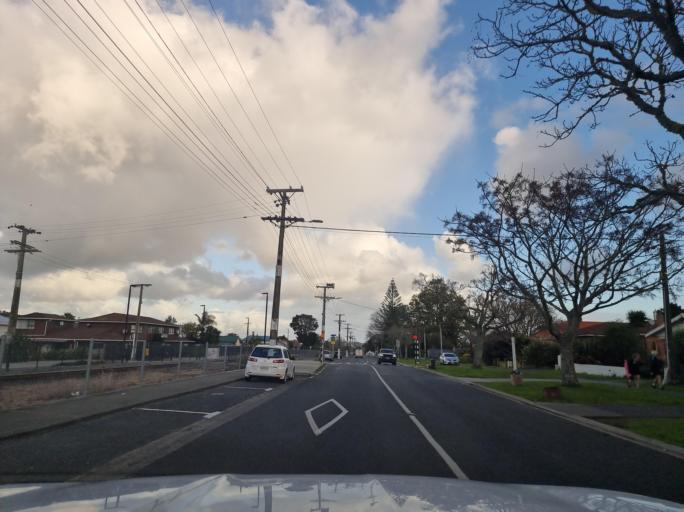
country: NZ
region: Northland
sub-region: Whangarei
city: Whangarei
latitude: -35.7107
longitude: 174.3191
